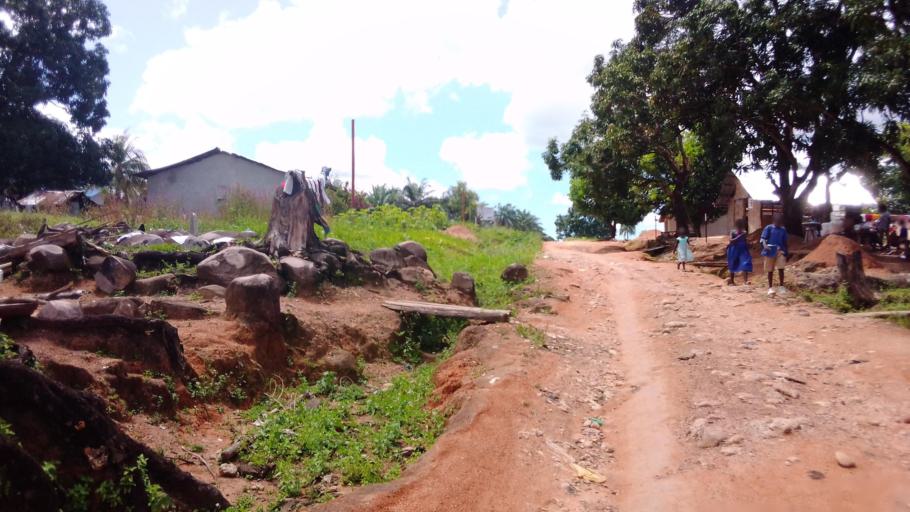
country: SL
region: Northern Province
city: Makeni
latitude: 8.8753
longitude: -12.0104
